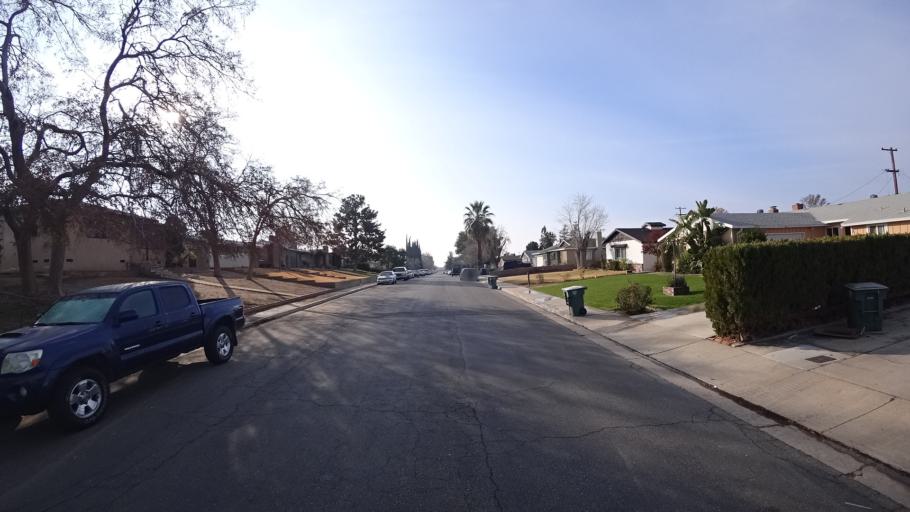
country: US
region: California
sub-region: Kern County
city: Oildale
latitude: 35.4017
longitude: -118.9715
